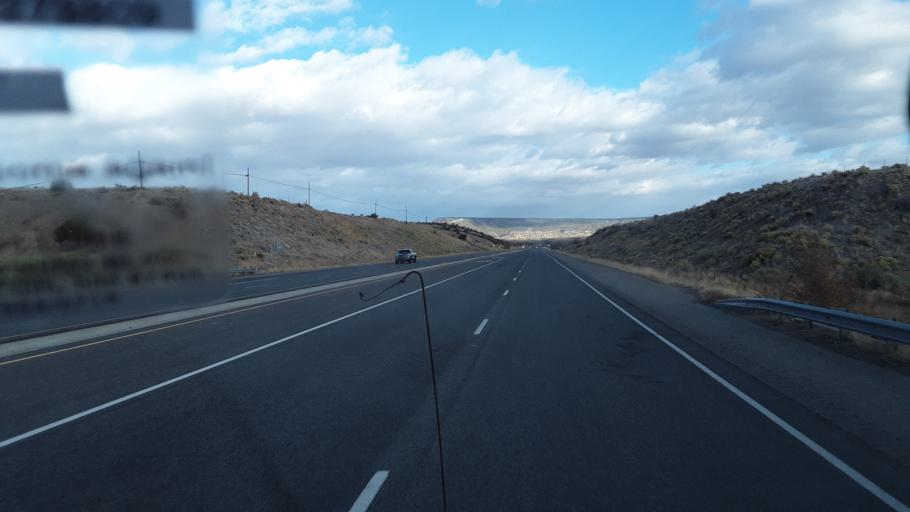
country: US
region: New Mexico
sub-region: Rio Arriba County
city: Espanola
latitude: 36.0237
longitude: -106.0916
